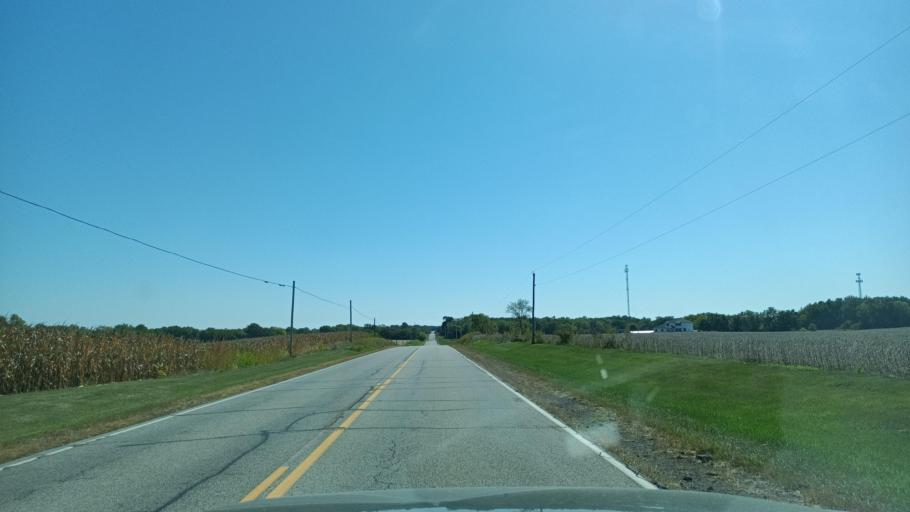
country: US
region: Illinois
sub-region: Peoria County
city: Elmwood
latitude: 40.8502
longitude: -89.9159
